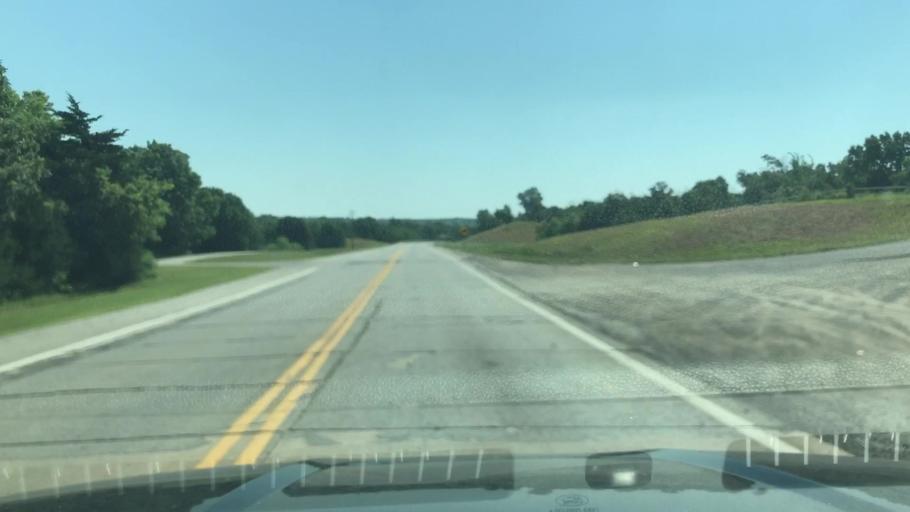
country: US
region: Oklahoma
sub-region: Creek County
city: Drumright
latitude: 35.9873
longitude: -96.5790
